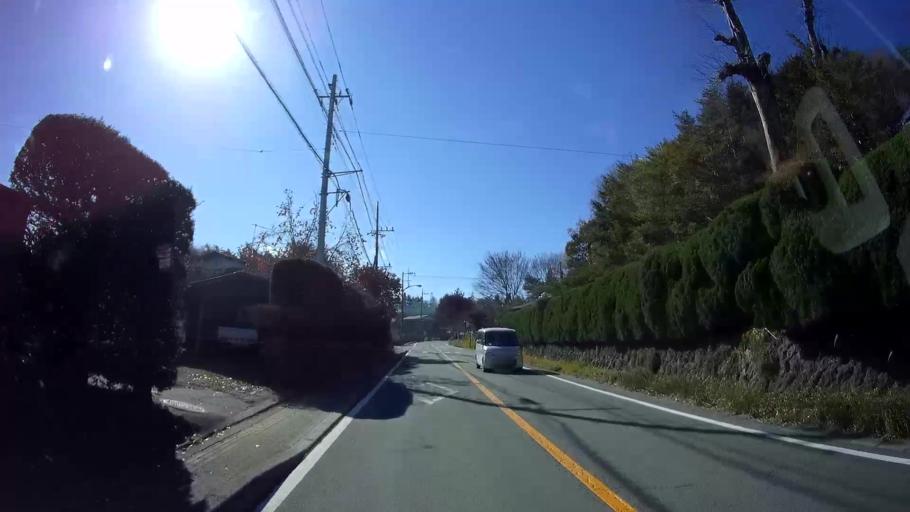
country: JP
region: Yamanashi
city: Fujikawaguchiko
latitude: 35.4952
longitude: 138.7313
